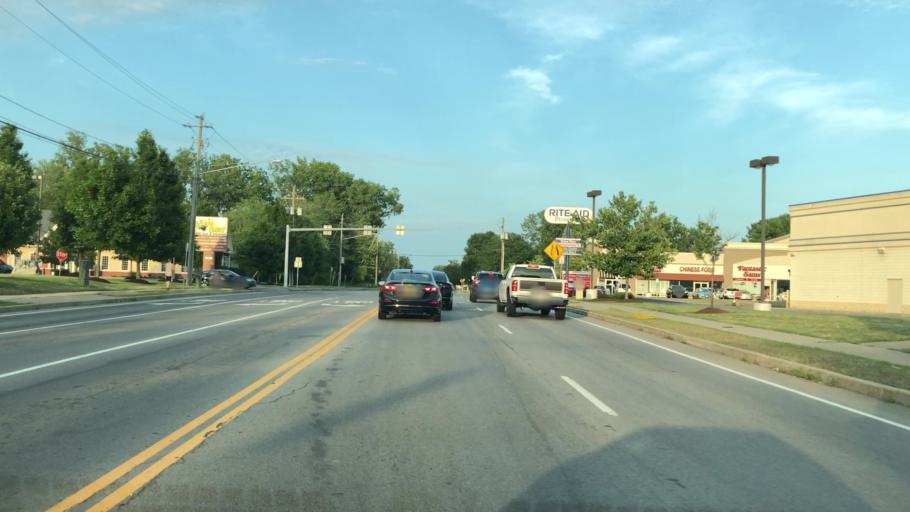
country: US
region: New York
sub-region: Erie County
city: Cheektowaga
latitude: 42.8823
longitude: -78.7536
